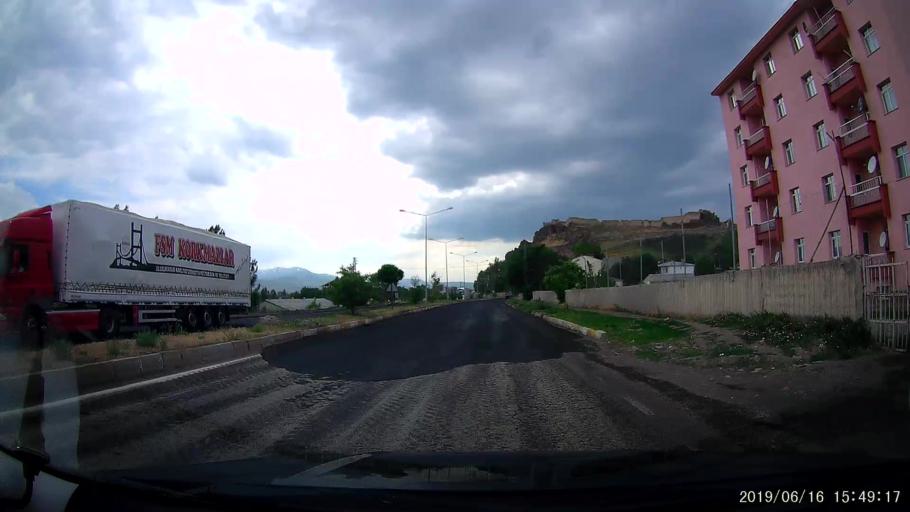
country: TR
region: Erzurum
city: Pasinler
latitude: 39.9789
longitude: 41.6886
